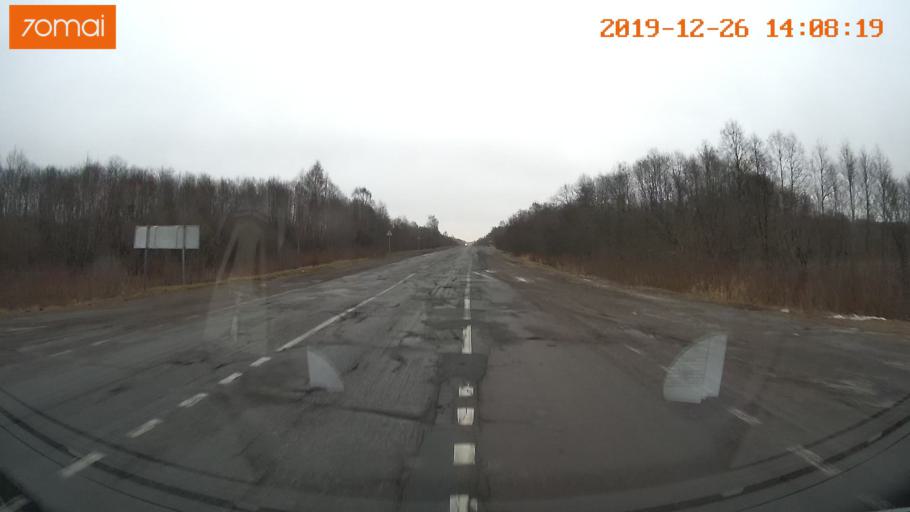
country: RU
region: Jaroslavl
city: Poshekhon'ye
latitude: 58.5086
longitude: 38.9098
